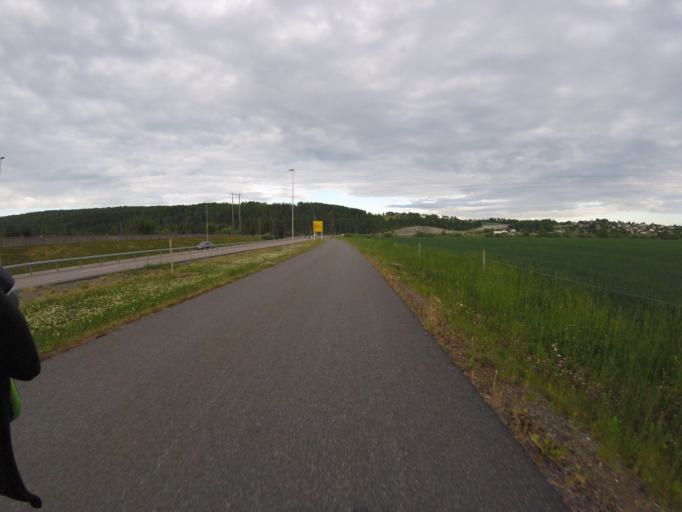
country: NO
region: Akershus
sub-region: Fet
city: Fetsund
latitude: 59.9409
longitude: 11.1219
